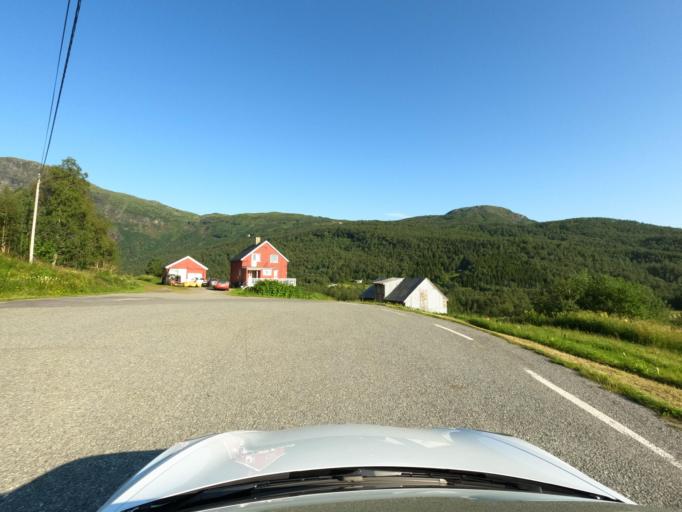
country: NO
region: Troms
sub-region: Gratangen
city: Gratangen
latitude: 68.5573
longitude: 17.7385
